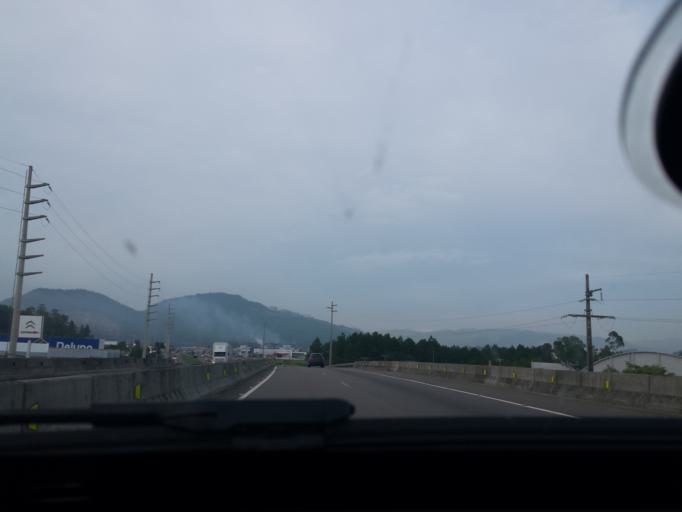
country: BR
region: Santa Catarina
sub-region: Tubarao
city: Tubarao
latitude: -28.4705
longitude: -49.0189
